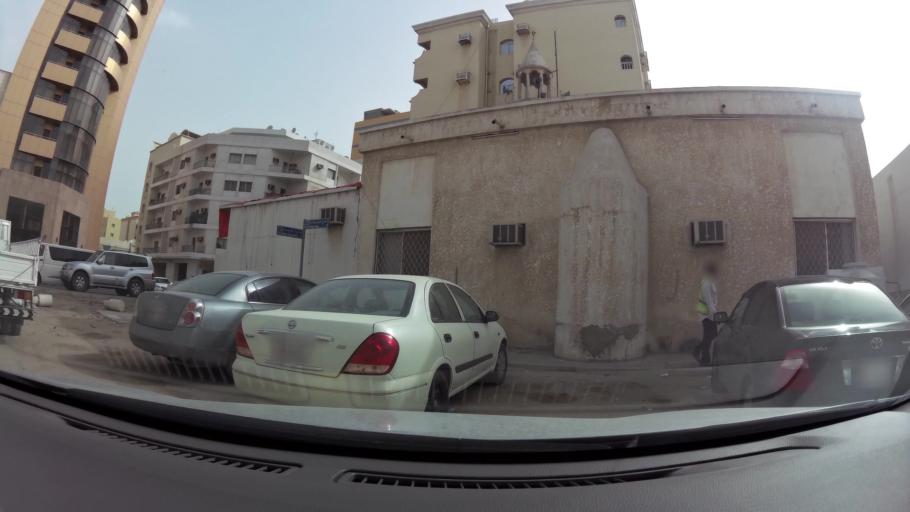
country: QA
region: Baladiyat ad Dawhah
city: Doha
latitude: 25.2805
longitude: 51.5487
